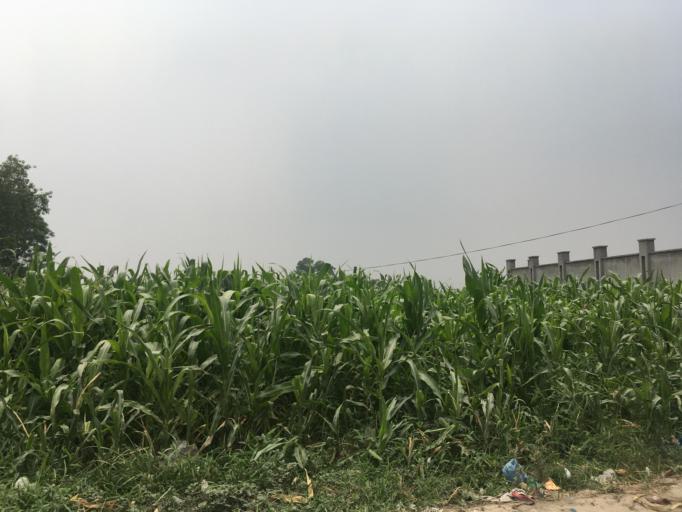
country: PK
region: Punjab
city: Lahore
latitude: 31.6192
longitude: 74.3538
